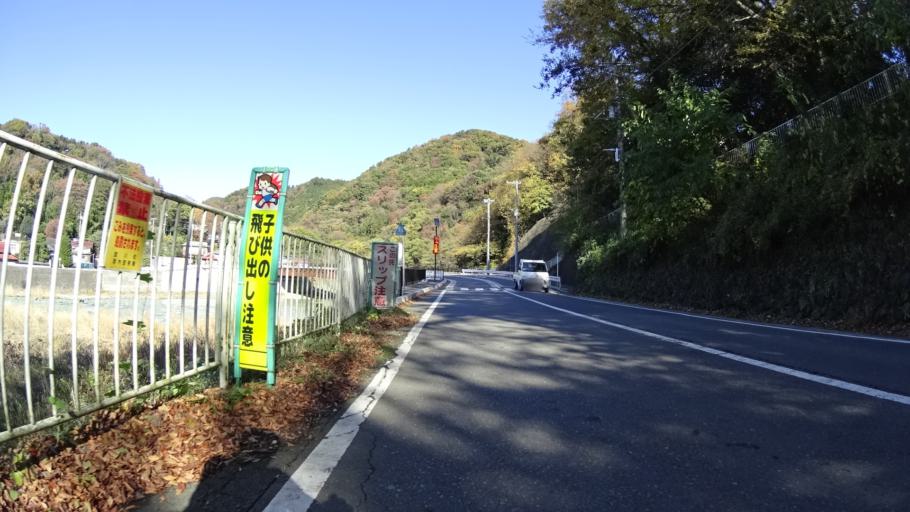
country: JP
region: Kanagawa
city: Zama
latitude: 35.5309
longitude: 139.2854
